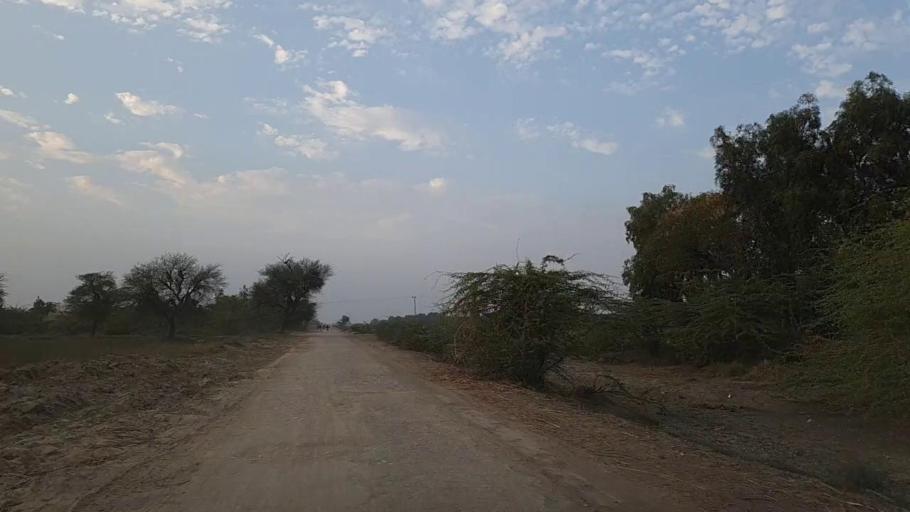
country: PK
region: Sindh
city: Mirwah Gorchani
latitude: 25.3185
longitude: 69.2210
